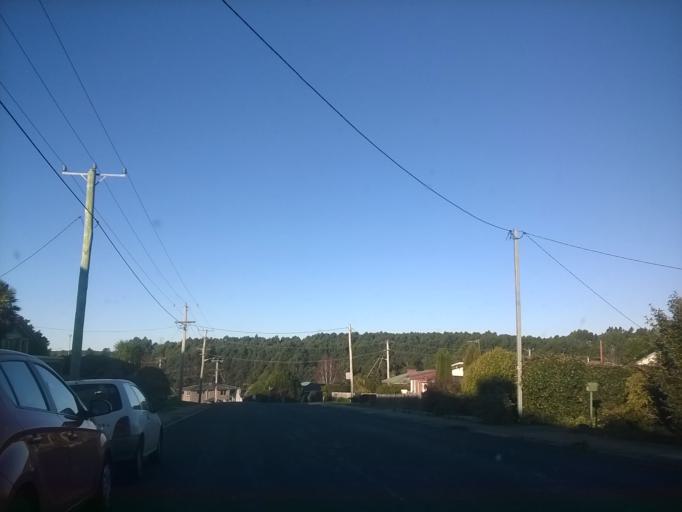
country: AU
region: Tasmania
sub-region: Burnie
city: Burnie
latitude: -41.0768
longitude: 145.9043
